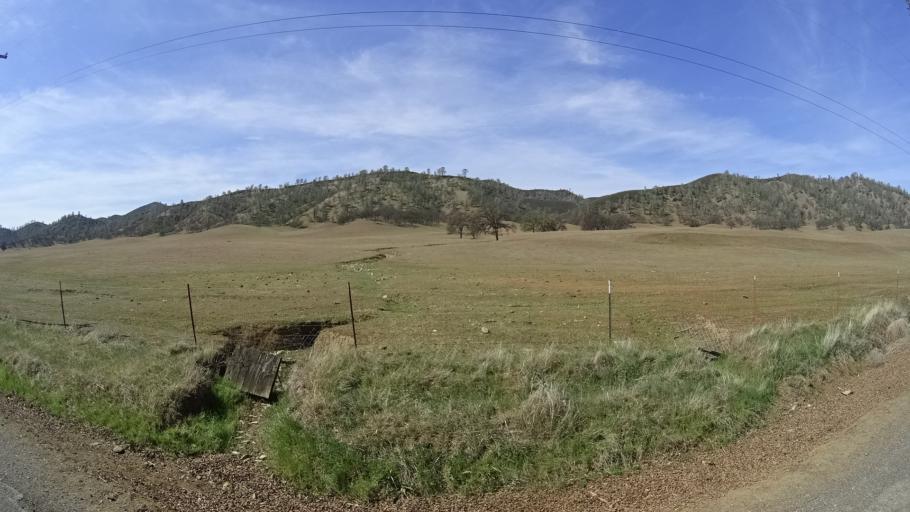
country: US
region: California
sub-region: Glenn County
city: Willows
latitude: 39.4742
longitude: -122.4481
